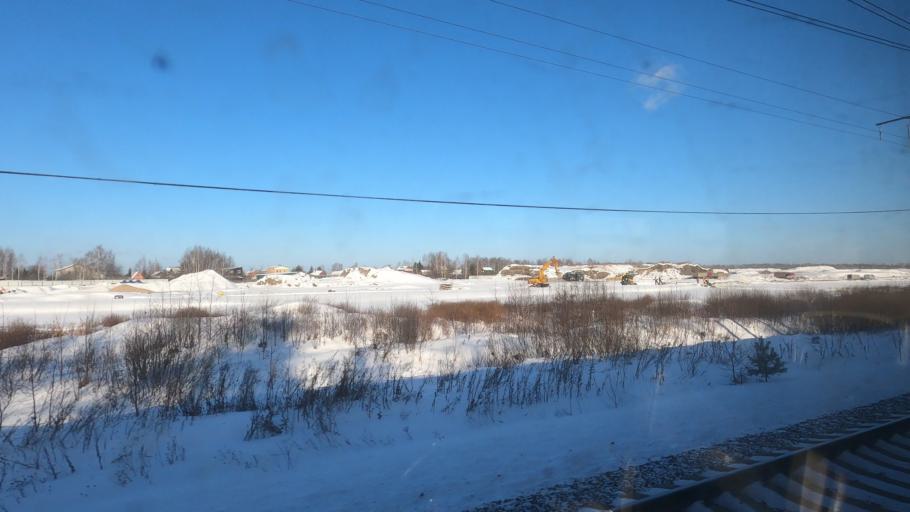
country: RU
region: Moskovskaya
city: Elektrougli
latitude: 55.7229
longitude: 38.2562
